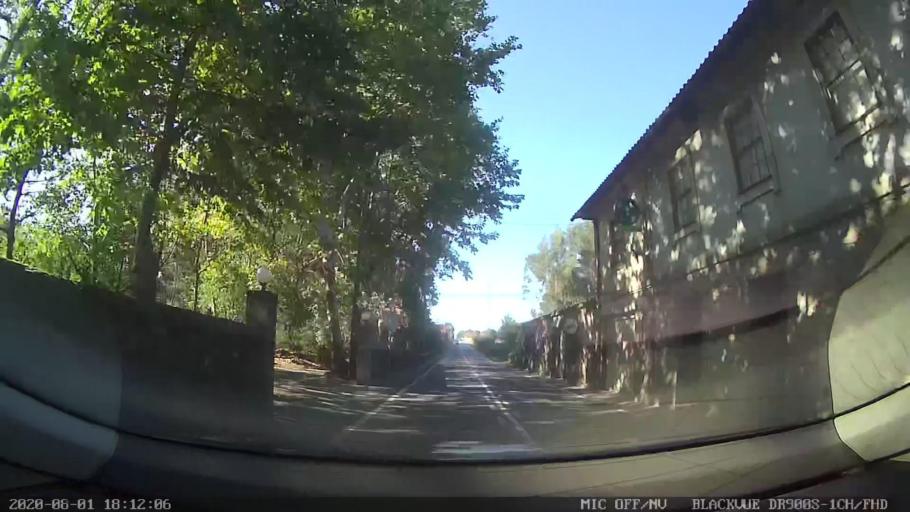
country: PT
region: Porto
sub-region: Santo Tirso
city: Sao Miguel do Couto
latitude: 41.2922
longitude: -8.4711
